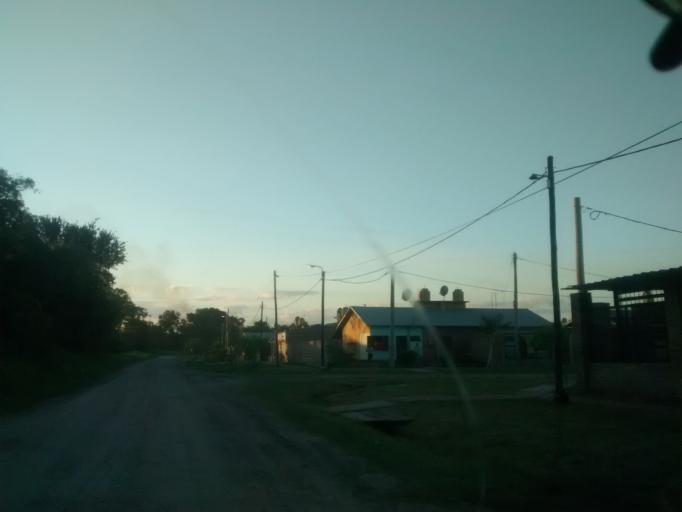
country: AR
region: Chaco
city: Fontana
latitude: -27.4043
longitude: -58.9914
